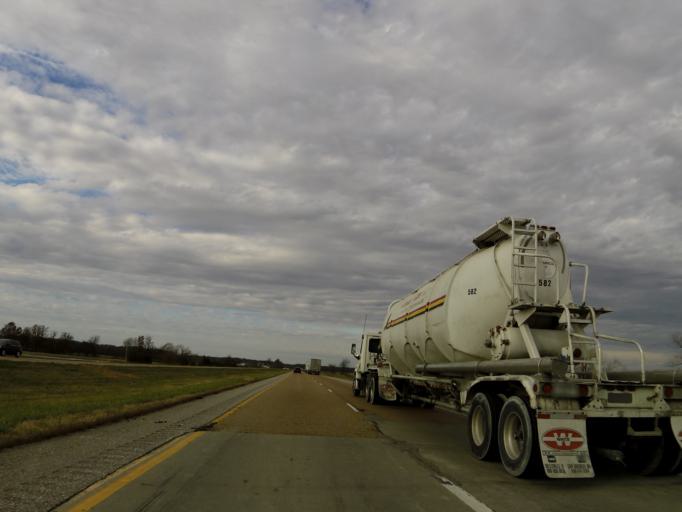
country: US
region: Illinois
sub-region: Washington County
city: Nashville
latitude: 38.3912
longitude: -89.2753
